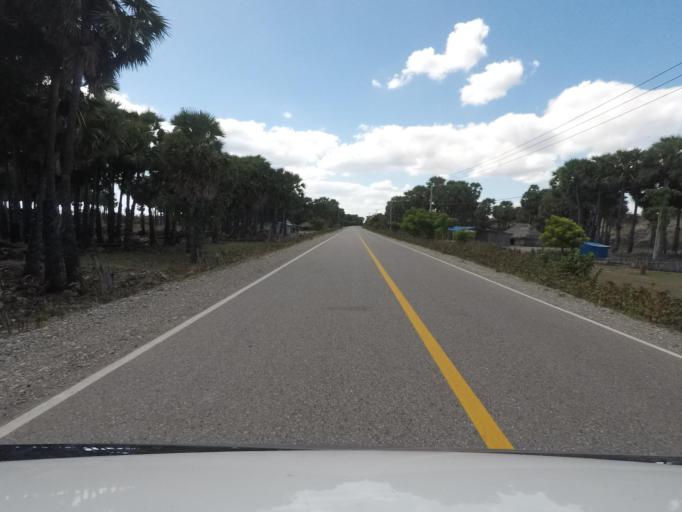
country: TL
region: Baucau
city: Baucau
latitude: -8.4332
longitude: 126.6743
